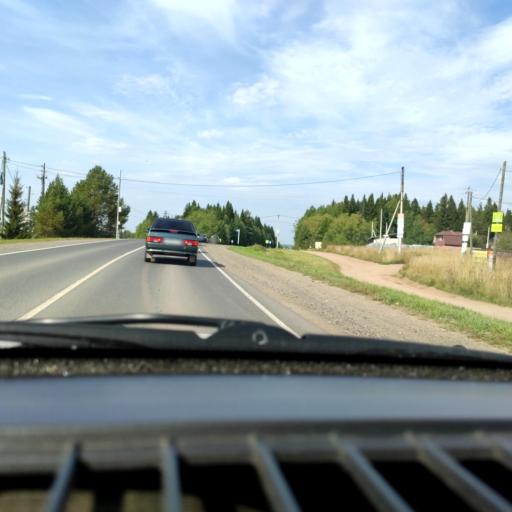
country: RU
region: Perm
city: Ust'-Kachka
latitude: 57.9190
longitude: 55.7648
